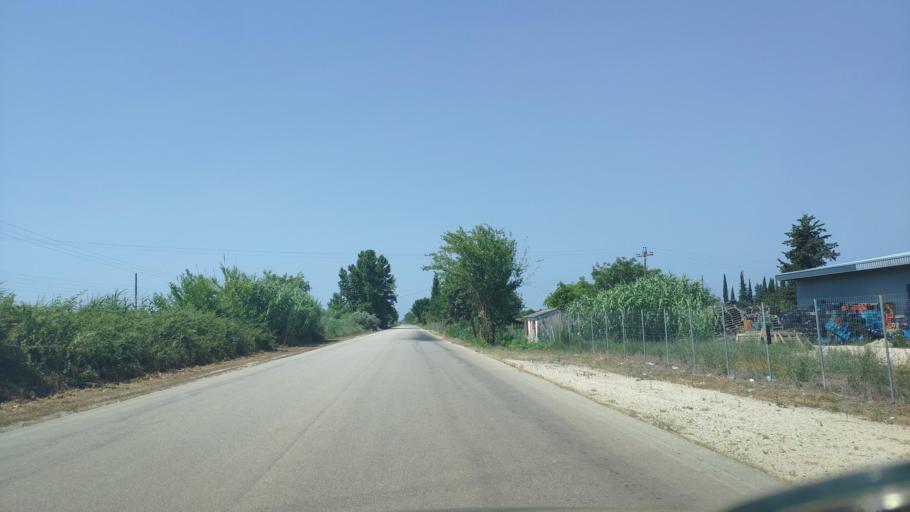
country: GR
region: Epirus
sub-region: Nomos Artas
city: Aneza
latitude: 39.1138
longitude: 20.9274
